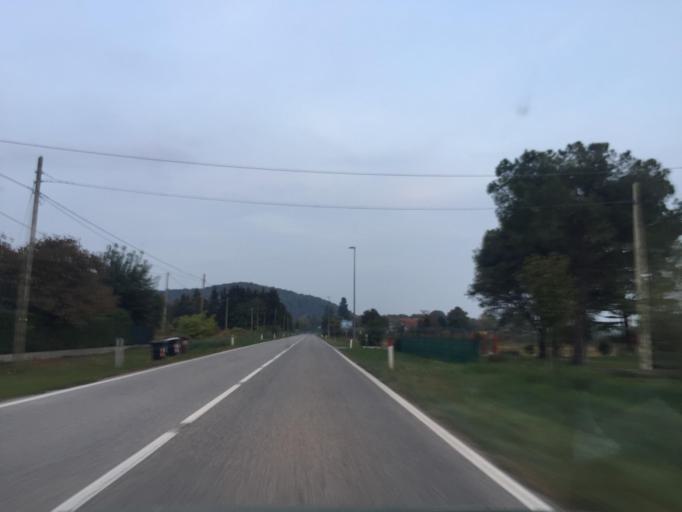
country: IT
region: Friuli Venezia Giulia
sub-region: Provincia di Pordenone
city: Arba
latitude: 46.1623
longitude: 12.8009
